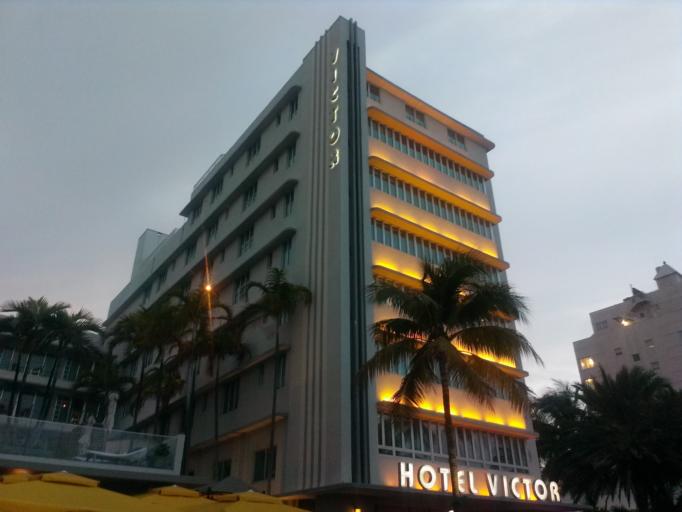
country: US
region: Florida
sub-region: Miami-Dade County
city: Miami Beach
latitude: 25.7822
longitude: -80.1302
